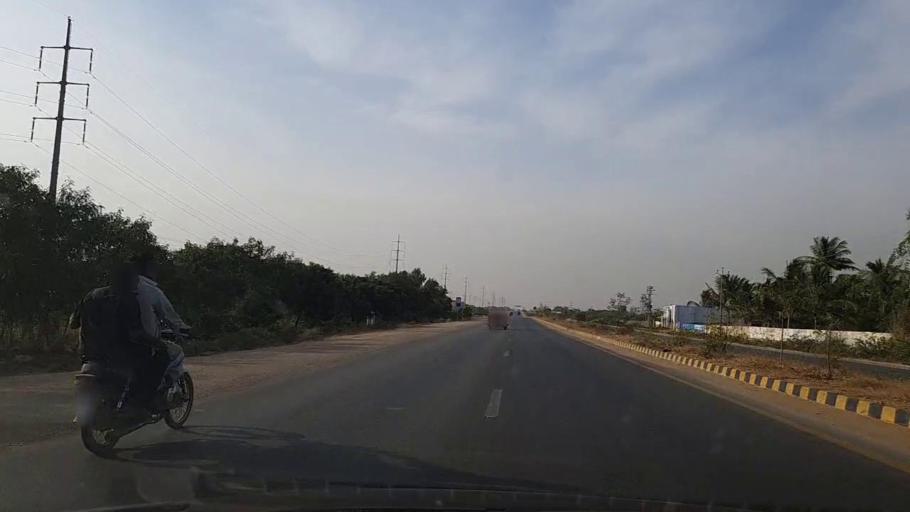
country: PK
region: Sindh
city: Gharo
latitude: 24.7574
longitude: 67.5615
